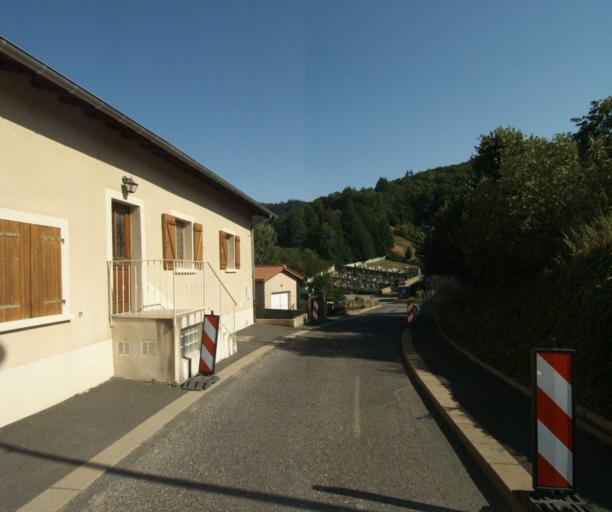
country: FR
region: Rhone-Alpes
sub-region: Departement du Rhone
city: Saint-Pierre-la-Palud
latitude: 45.7695
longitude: 4.6090
